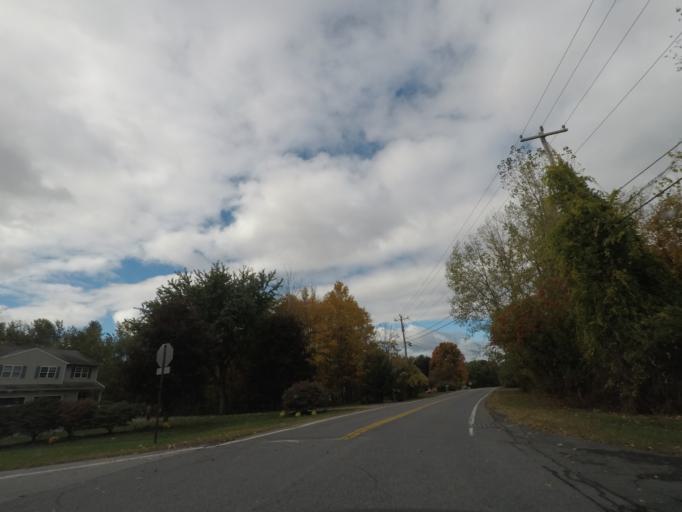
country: US
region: New York
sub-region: Saratoga County
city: Country Knolls
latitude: 42.8802
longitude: -73.7518
